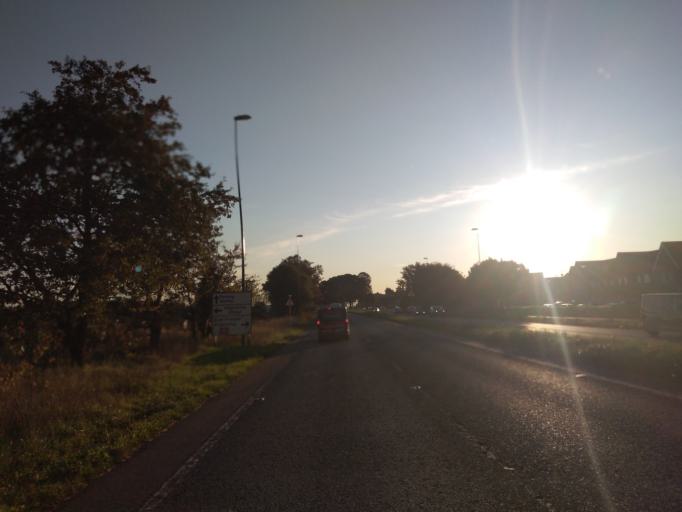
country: GB
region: England
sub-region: West Sussex
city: Rustington
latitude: 50.8184
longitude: -0.4924
